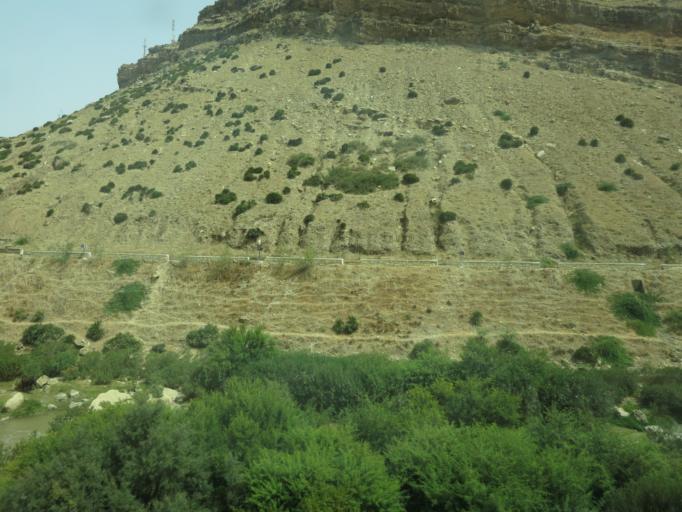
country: MA
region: Gharb-Chrarda-Beni Hssen
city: Sidi Qacem
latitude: 34.1840
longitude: -5.7081
